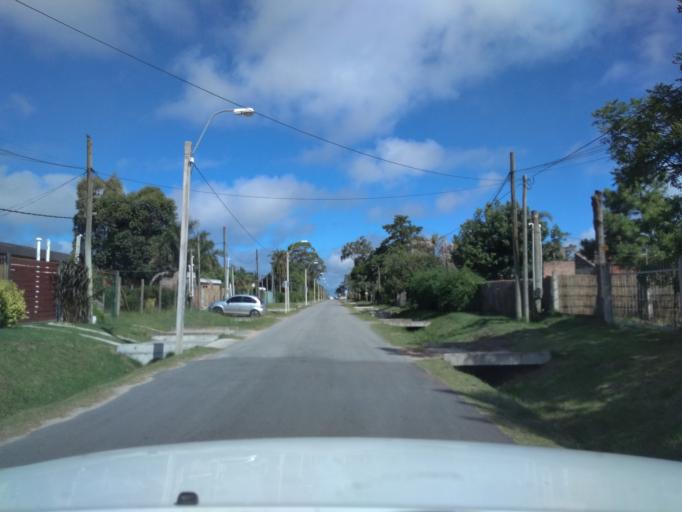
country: UY
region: Canelones
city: Barra de Carrasco
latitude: -34.8355
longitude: -55.9713
